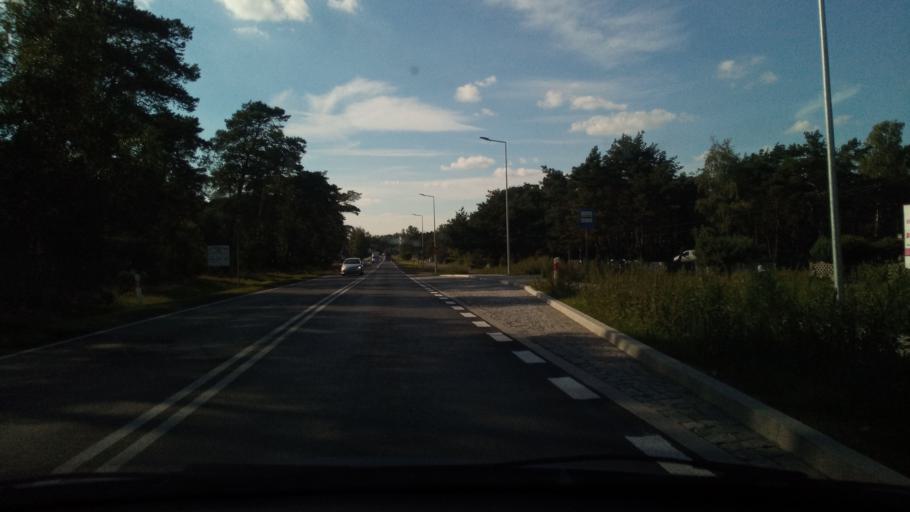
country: PL
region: Lodz Voivodeship
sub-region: Powiat piotrkowski
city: Sulejow
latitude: 51.3717
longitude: 19.8317
